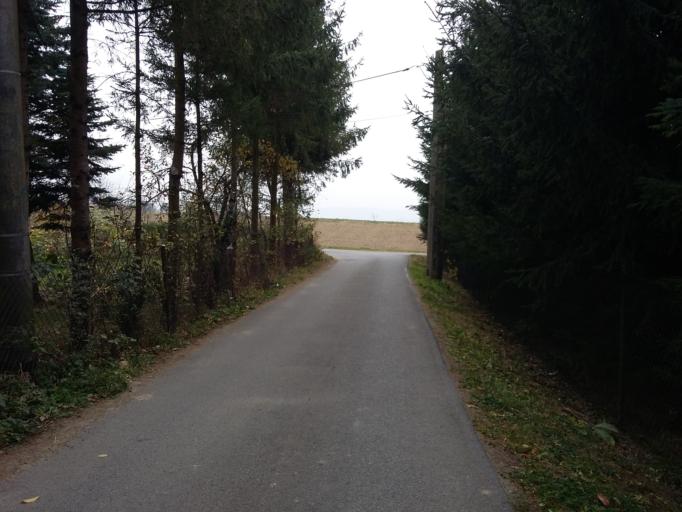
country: PL
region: Subcarpathian Voivodeship
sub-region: Powiat jasielski
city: Tarnowiec
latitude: 49.7325
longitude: 21.5723
